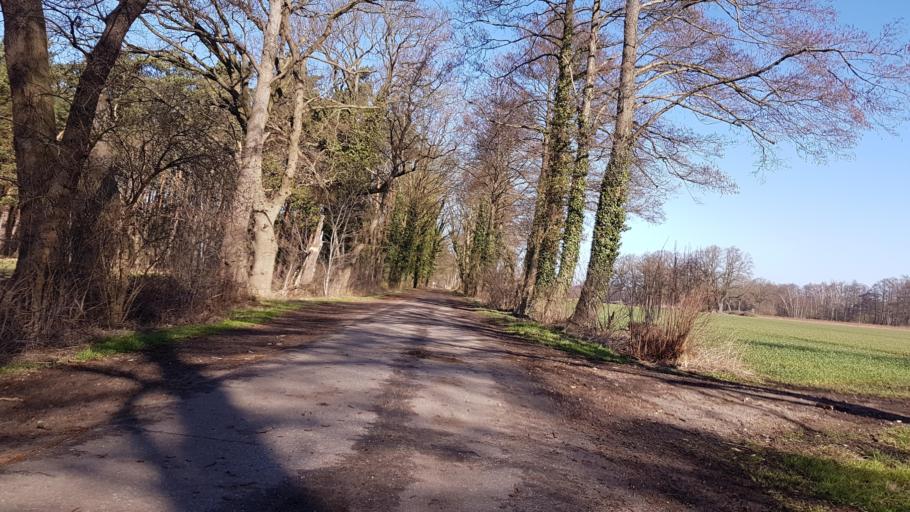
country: DE
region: Lower Saxony
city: Garbsen-Mitte
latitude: 52.4520
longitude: 9.6370
